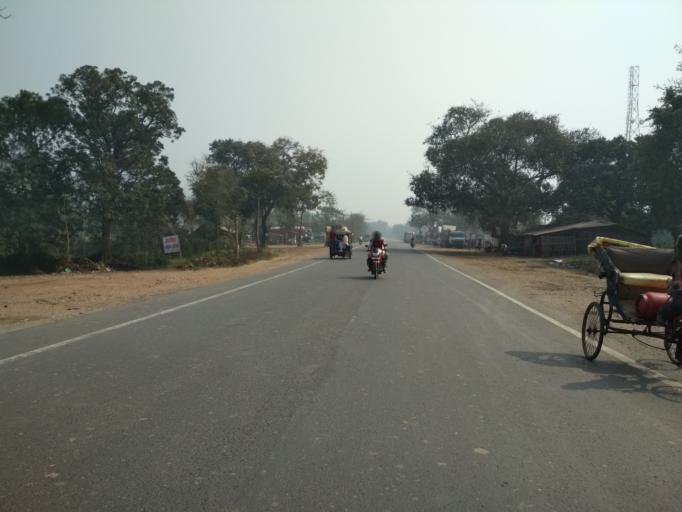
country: IN
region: Bihar
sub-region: Khagaria
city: Khagaria
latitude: 25.5074
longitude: 86.5829
